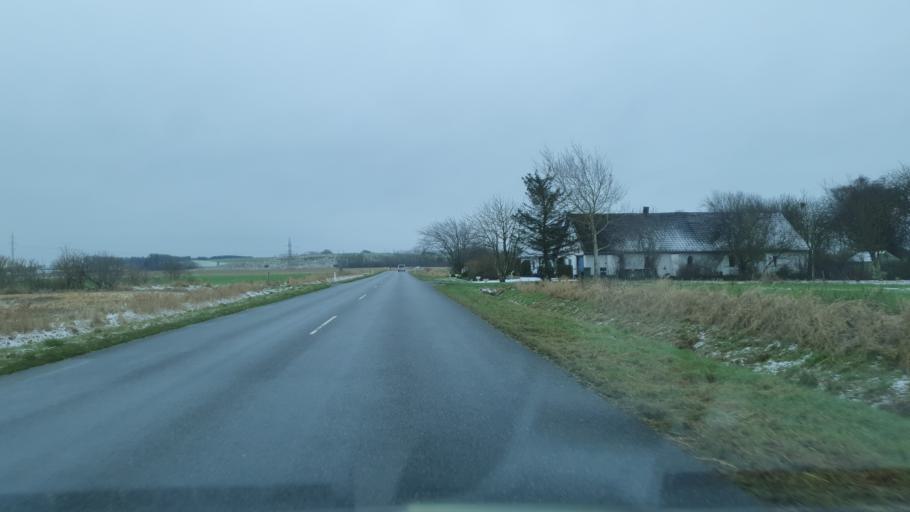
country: DK
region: North Denmark
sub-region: Jammerbugt Kommune
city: Brovst
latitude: 57.1190
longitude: 9.4966
